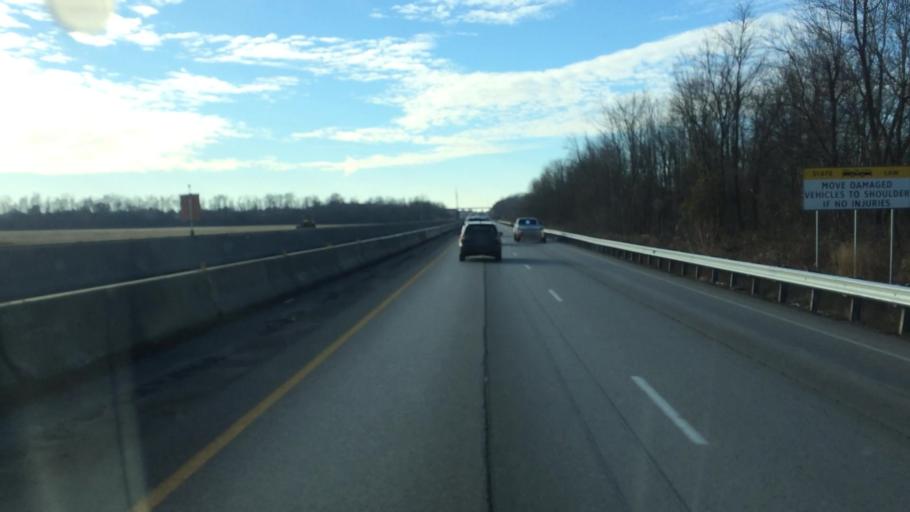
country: US
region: Kentucky
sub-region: Hardin County
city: Elizabethtown
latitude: 37.5686
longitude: -85.8748
